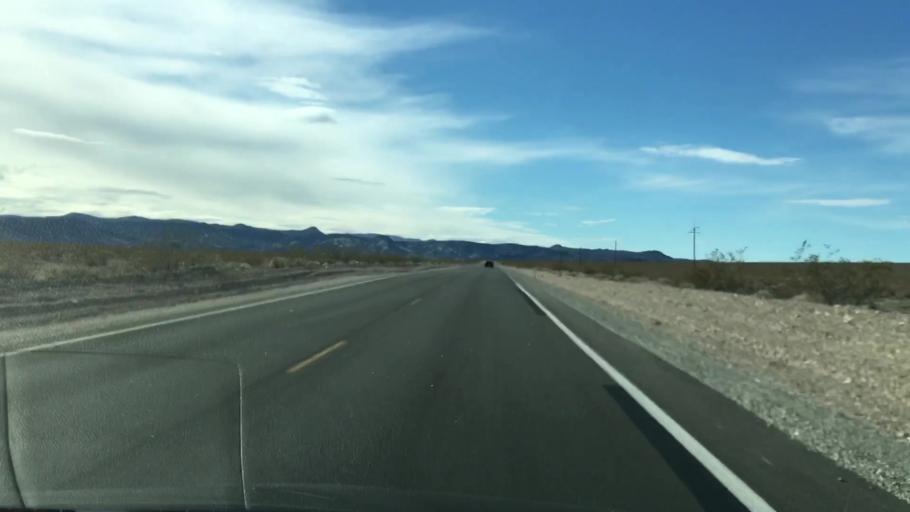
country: US
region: Nevada
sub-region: Nye County
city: Pahrump
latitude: 36.3034
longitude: -116.4865
